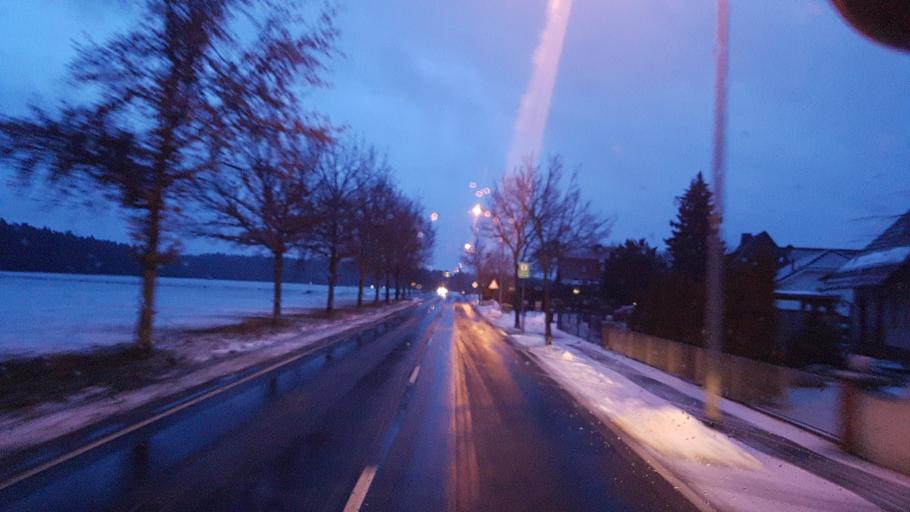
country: DE
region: Brandenburg
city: Briesen
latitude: 51.8095
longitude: 14.2468
